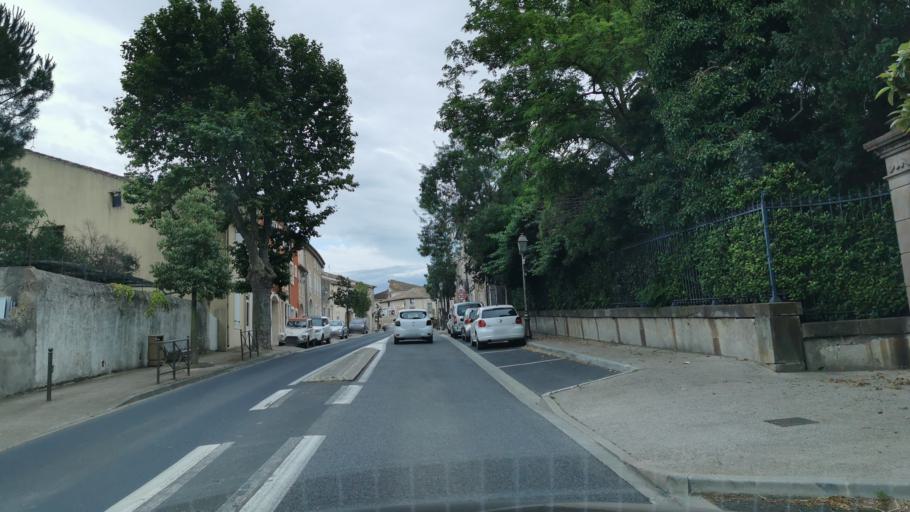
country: FR
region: Languedoc-Roussillon
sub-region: Departement de l'Aude
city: Marcorignan
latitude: 43.2271
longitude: 2.9225
